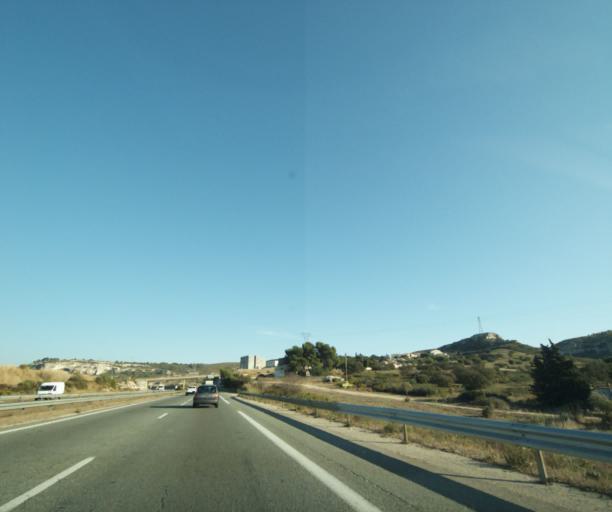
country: FR
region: Provence-Alpes-Cote d'Azur
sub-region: Departement des Bouches-du-Rhone
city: Gignac-la-Nerthe
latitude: 43.3804
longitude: 5.2151
